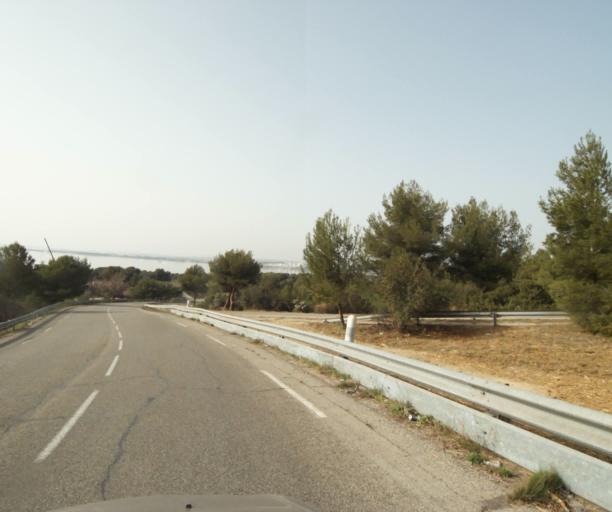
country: FR
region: Provence-Alpes-Cote d'Azur
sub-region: Departement des Bouches-du-Rhone
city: Vitrolles
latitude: 43.4675
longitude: 5.2368
